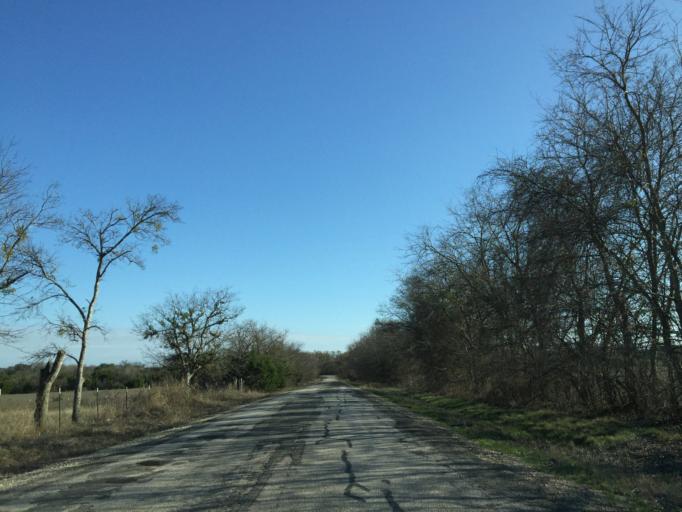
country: US
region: Texas
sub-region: Williamson County
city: Florence
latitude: 30.7746
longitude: -97.8385
